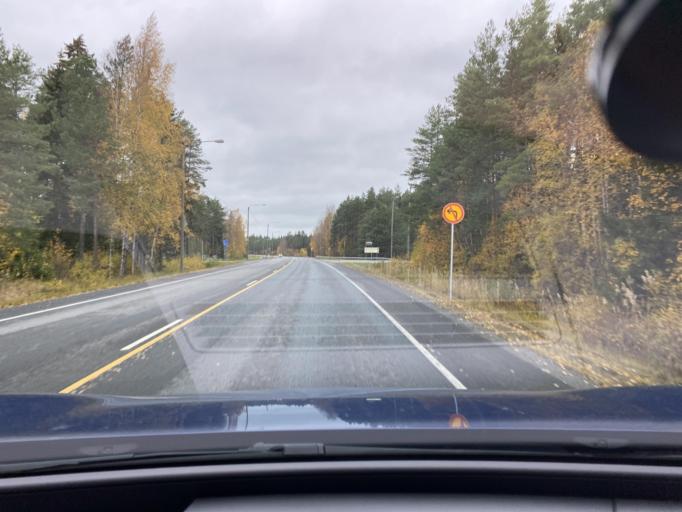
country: FI
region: Satakunta
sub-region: Rauma
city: Rauma
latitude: 61.1338
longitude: 21.5941
